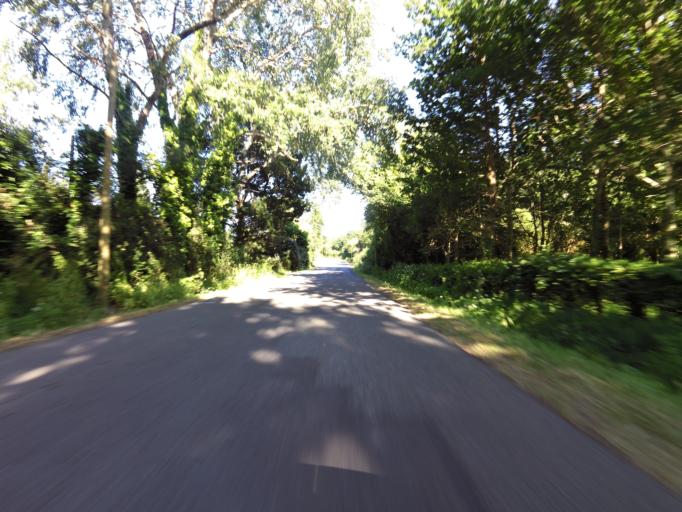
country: FR
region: Brittany
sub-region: Departement du Morbihan
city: Penestin
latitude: 47.4726
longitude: -2.4758
